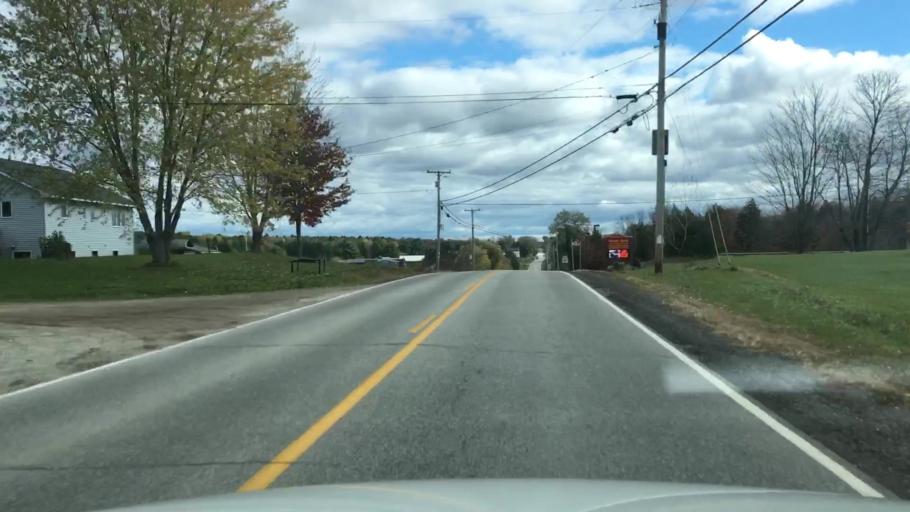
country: US
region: Maine
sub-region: Sagadahoc County
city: Richmond
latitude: 44.0961
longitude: -69.8495
